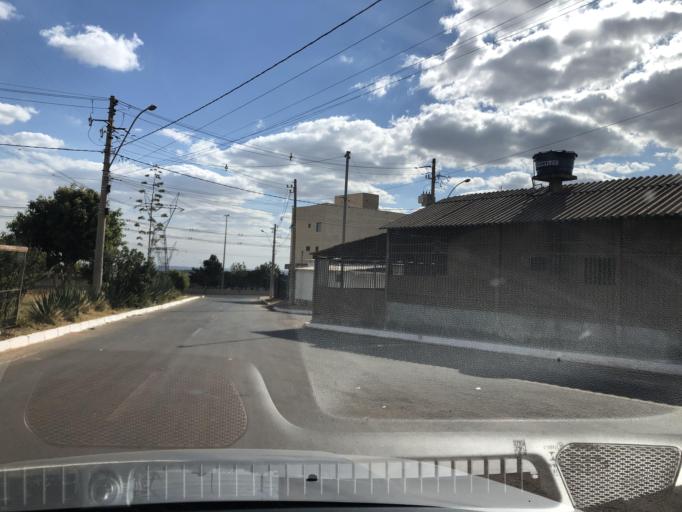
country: BR
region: Federal District
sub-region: Brasilia
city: Brasilia
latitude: -15.8912
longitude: -48.1264
